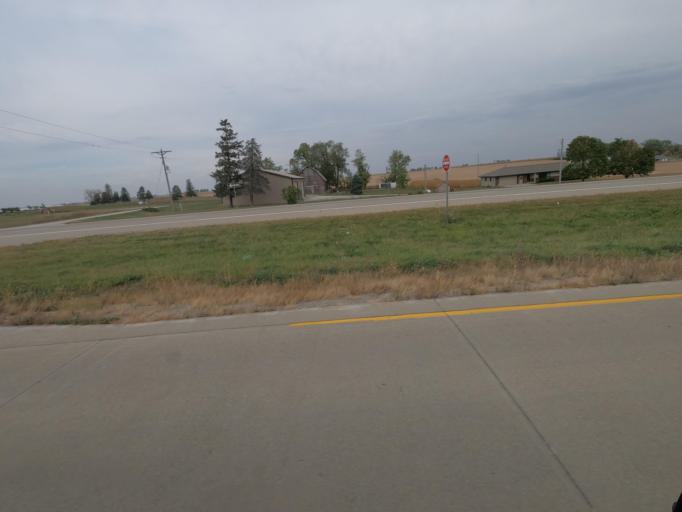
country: US
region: Iowa
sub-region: Marion County
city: Pella
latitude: 41.3894
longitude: -92.8523
